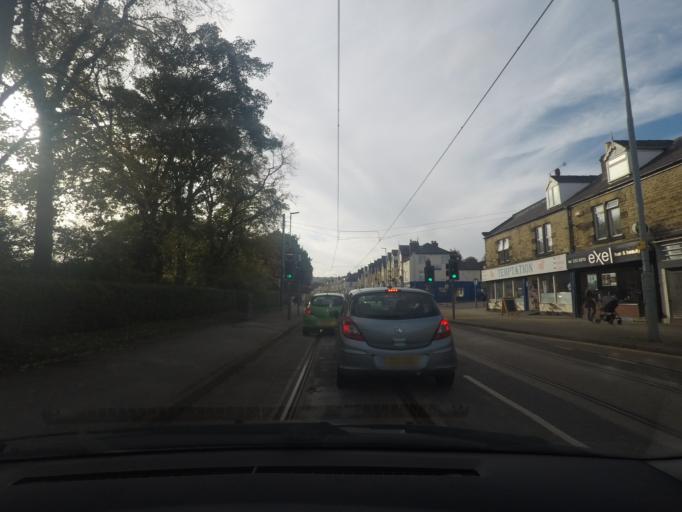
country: GB
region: England
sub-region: Sheffield
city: Sheffield
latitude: 53.4072
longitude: -1.5041
